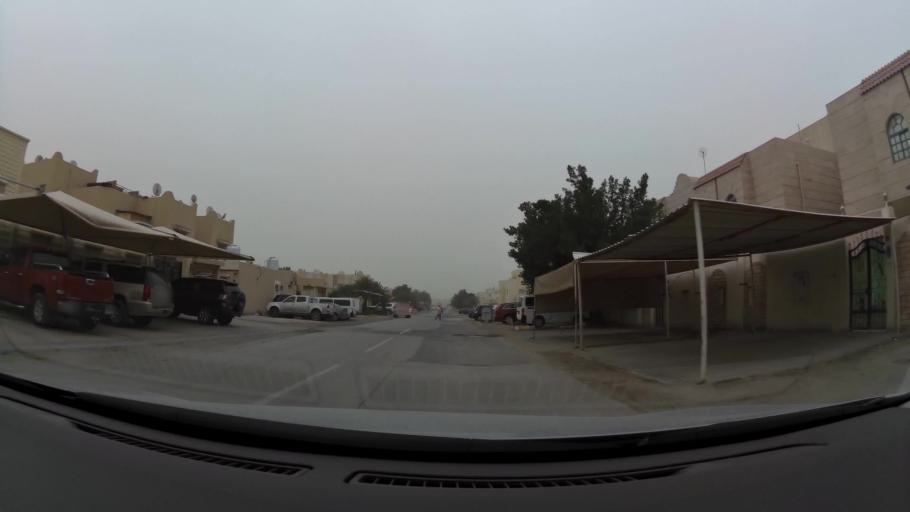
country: QA
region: Baladiyat ad Dawhah
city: Doha
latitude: 25.2318
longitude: 51.4985
